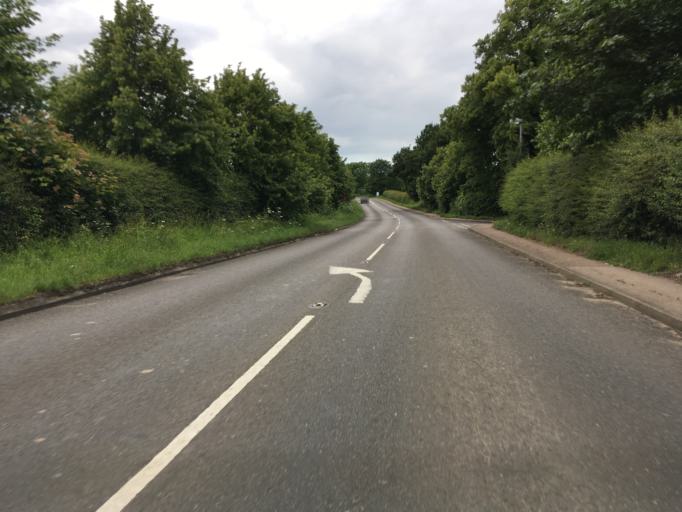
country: GB
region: England
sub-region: Central Bedfordshire
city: Woburn
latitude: 51.9925
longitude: -0.6229
